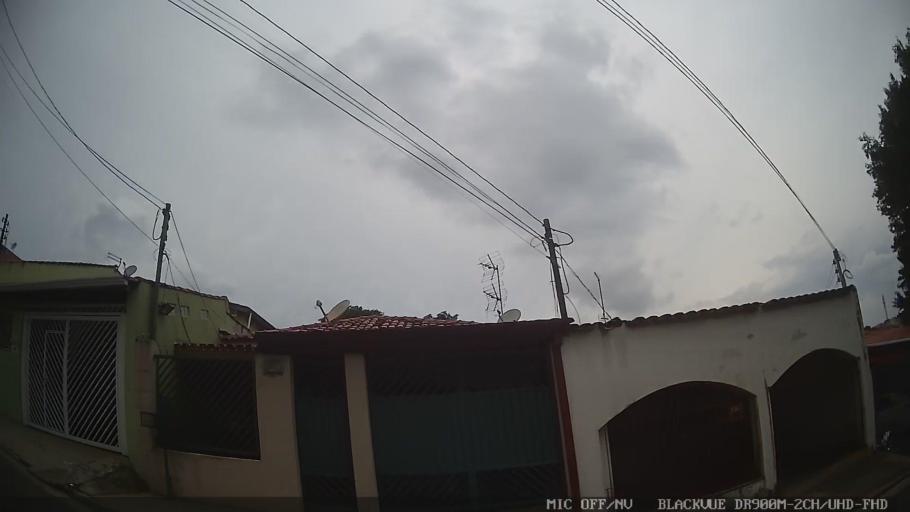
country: BR
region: Sao Paulo
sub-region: Atibaia
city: Atibaia
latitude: -23.1253
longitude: -46.5656
